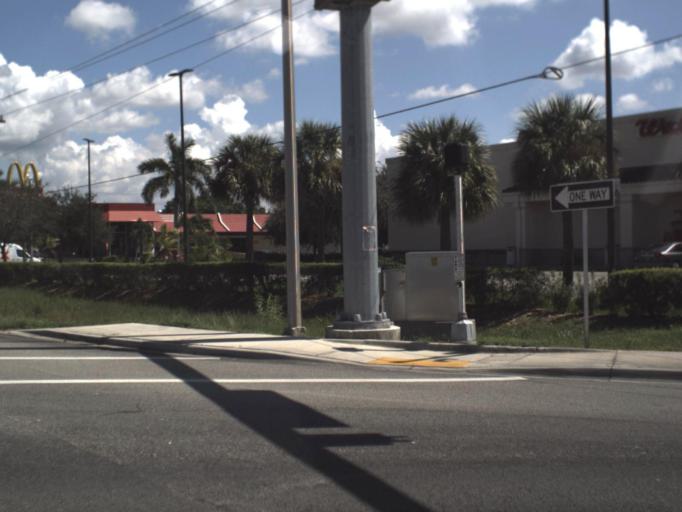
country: US
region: Florida
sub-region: Lee County
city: Lochmoor Waterway Estates
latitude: 26.6521
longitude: -81.9742
